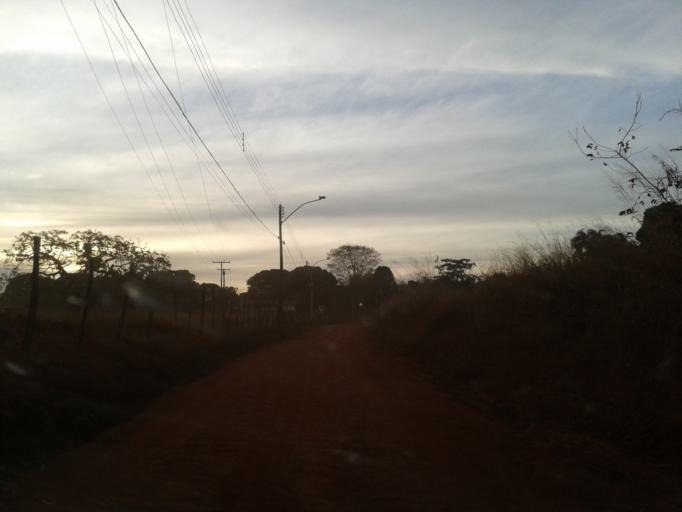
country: BR
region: Goias
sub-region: Goiania
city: Goiania
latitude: -16.6443
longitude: -49.3536
